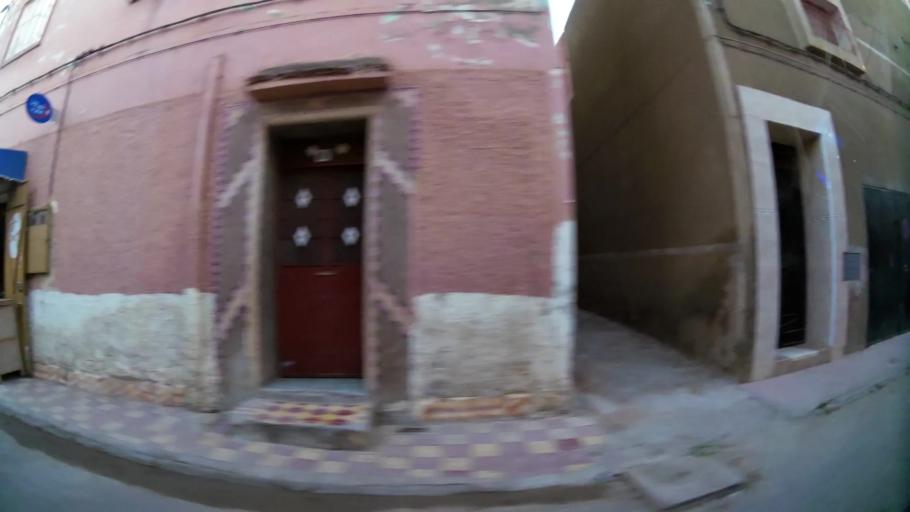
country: MA
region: Oriental
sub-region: Berkane-Taourirt
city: Berkane
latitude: 34.9197
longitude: -2.3160
